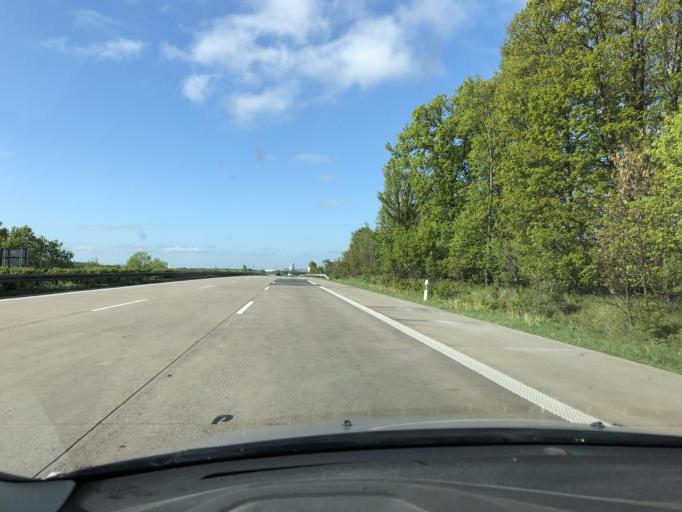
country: DE
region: Saxony-Anhalt
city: Osterfeld
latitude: 51.0596
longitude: 11.9494
